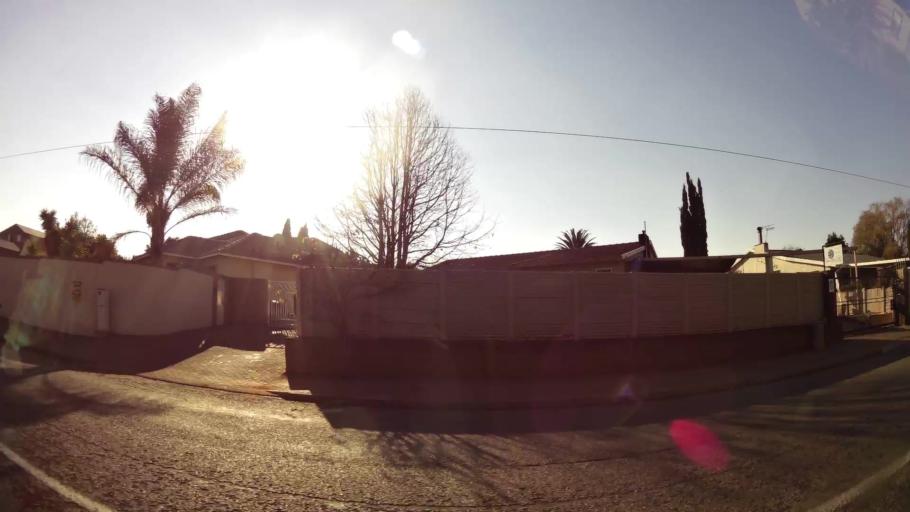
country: ZA
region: Gauteng
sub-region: City of Johannesburg Metropolitan Municipality
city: Modderfontein
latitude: -26.1405
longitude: 28.1655
